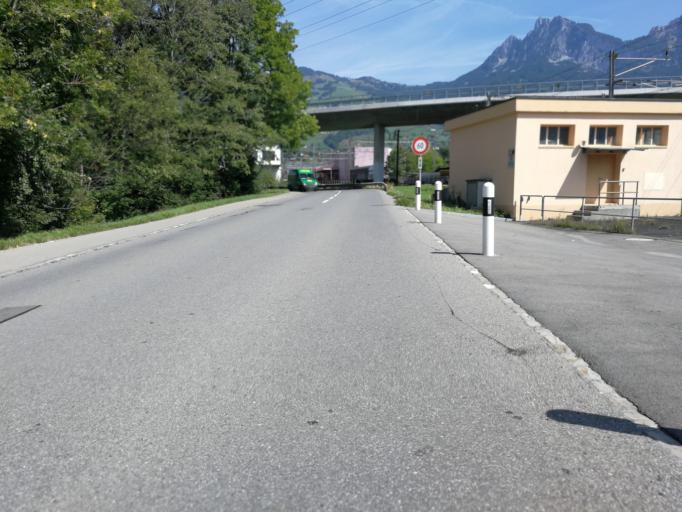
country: CH
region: Schwyz
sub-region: Bezirk Schwyz
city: Ingenbohl
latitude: 47.0178
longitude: 8.6278
